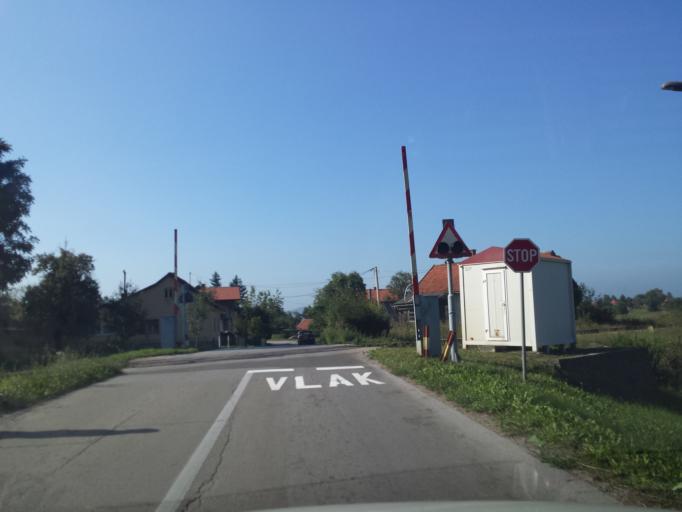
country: HR
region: Karlovacka
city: Ostarije
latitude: 45.2200
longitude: 15.2782
